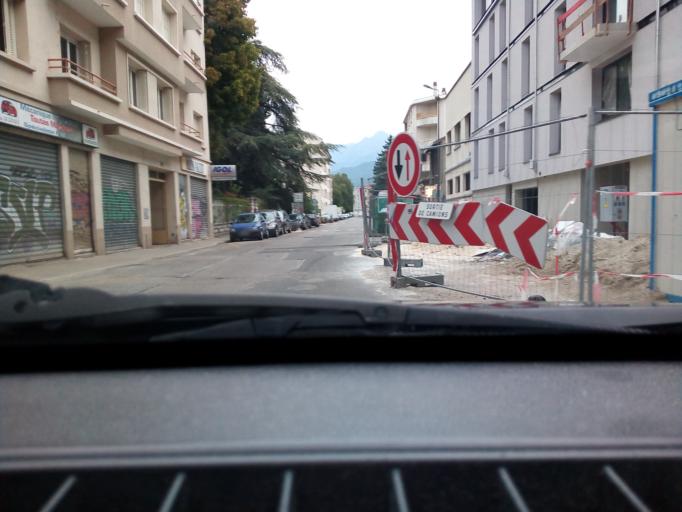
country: FR
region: Rhone-Alpes
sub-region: Departement de l'Isere
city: La Tronche
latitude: 45.1806
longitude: 5.7368
